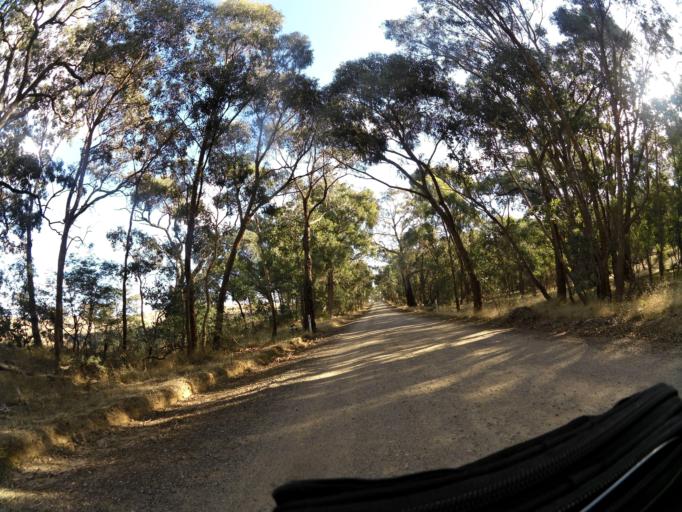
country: AU
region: Victoria
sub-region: Greater Bendigo
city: Kennington
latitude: -37.0202
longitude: 144.8040
